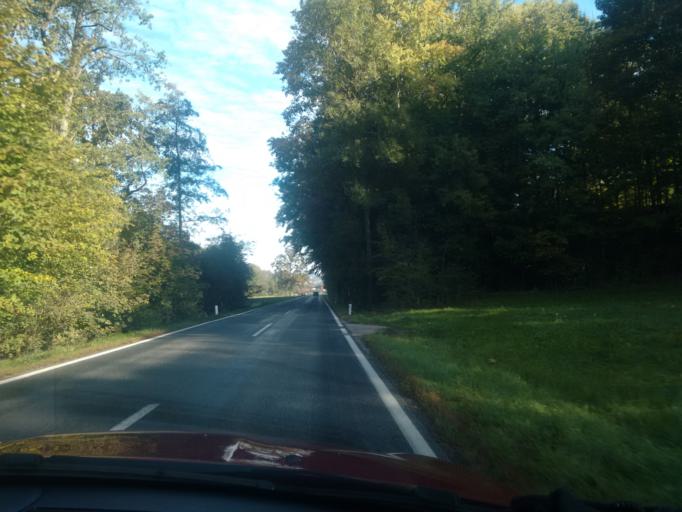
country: AT
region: Upper Austria
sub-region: Politischer Bezirk Vocklabruck
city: Manning
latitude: 48.0759
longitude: 13.6632
